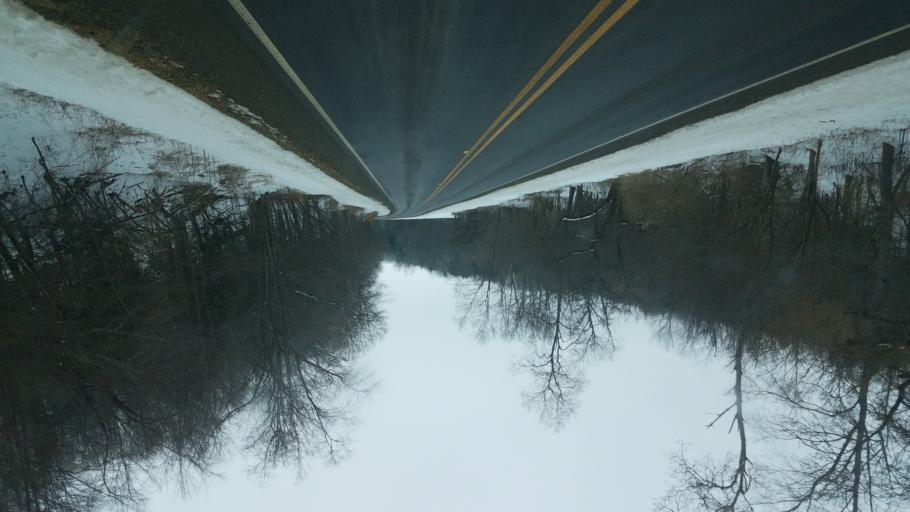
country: US
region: New York
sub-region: Allegany County
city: Andover
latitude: 42.0174
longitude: -77.7547
